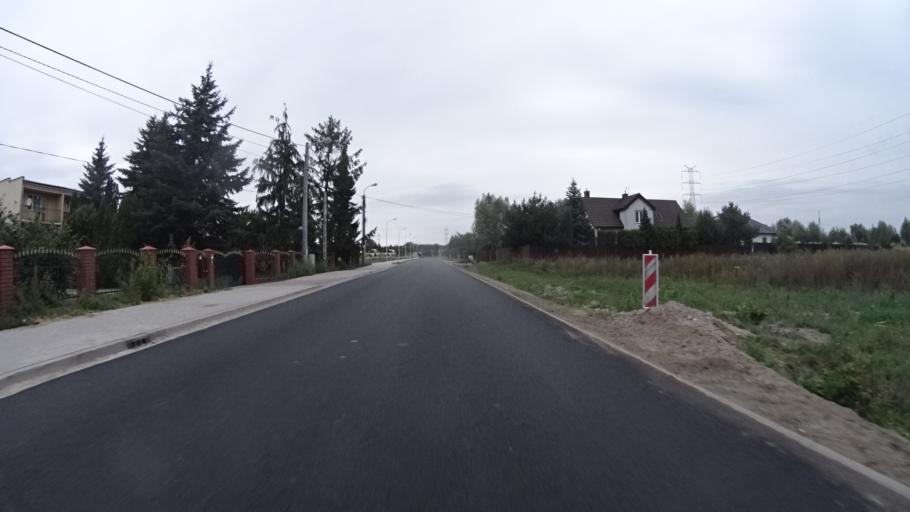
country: PL
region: Masovian Voivodeship
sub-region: Powiat warszawski zachodni
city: Stare Babice
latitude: 52.2653
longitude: 20.8258
